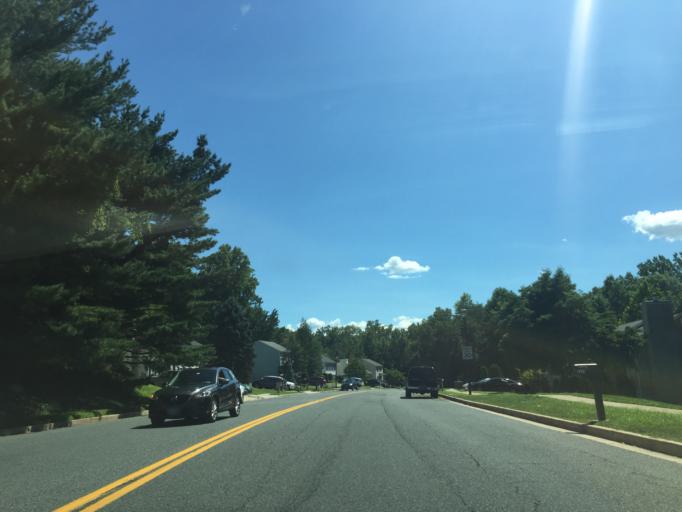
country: US
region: Maryland
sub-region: Baltimore County
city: Perry Hall
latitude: 39.4126
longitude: -76.4780
